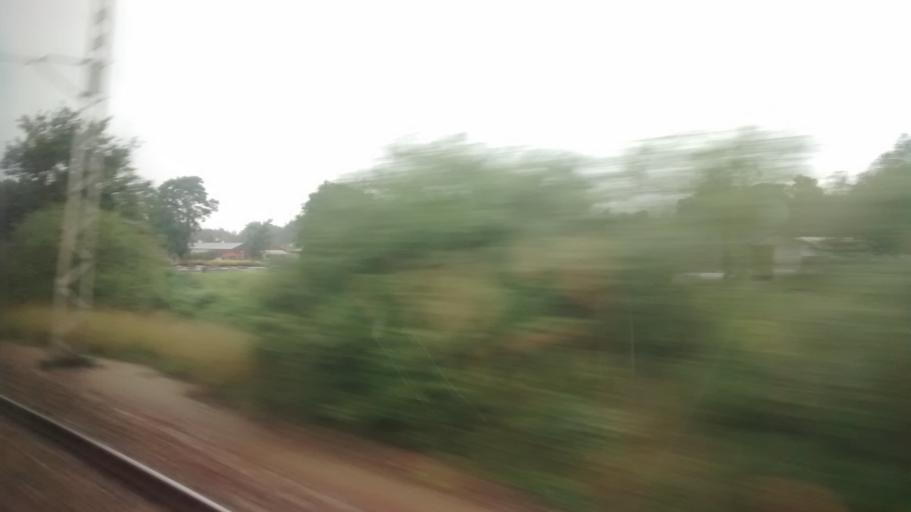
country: FR
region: Pays de la Loire
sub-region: Departement de la Sarthe
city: Saint-Mars-la-Briere
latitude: 48.0351
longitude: 0.3875
